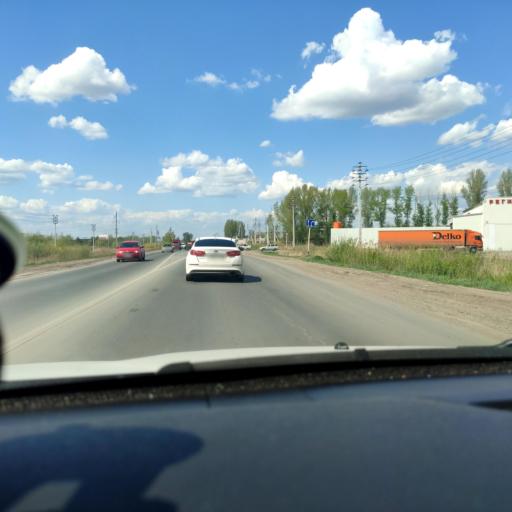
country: RU
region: Samara
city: Kinel'
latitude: 53.2297
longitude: 50.5913
